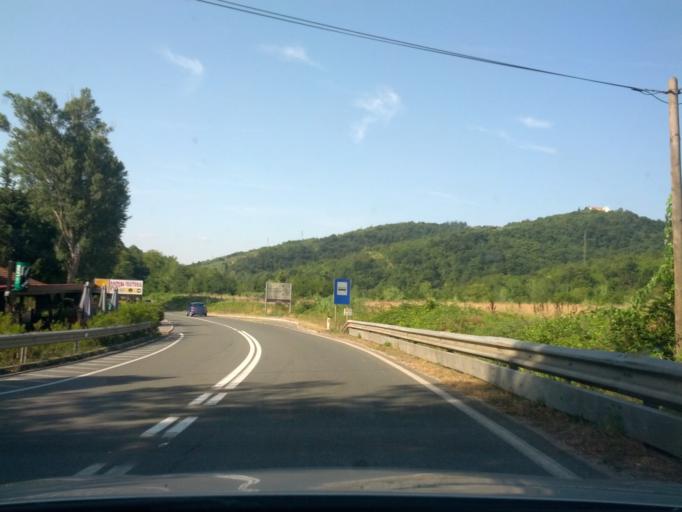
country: SI
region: Izola-Isola
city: Izola
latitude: 45.4964
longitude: 13.6785
